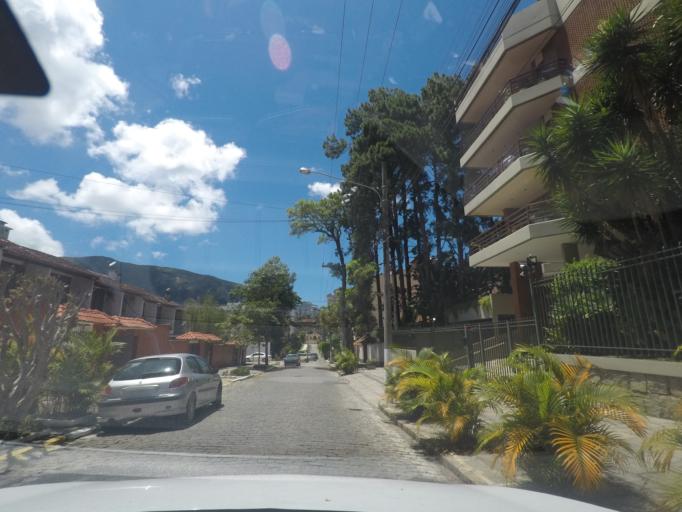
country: BR
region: Rio de Janeiro
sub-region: Teresopolis
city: Teresopolis
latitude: -22.4290
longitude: -42.9815
